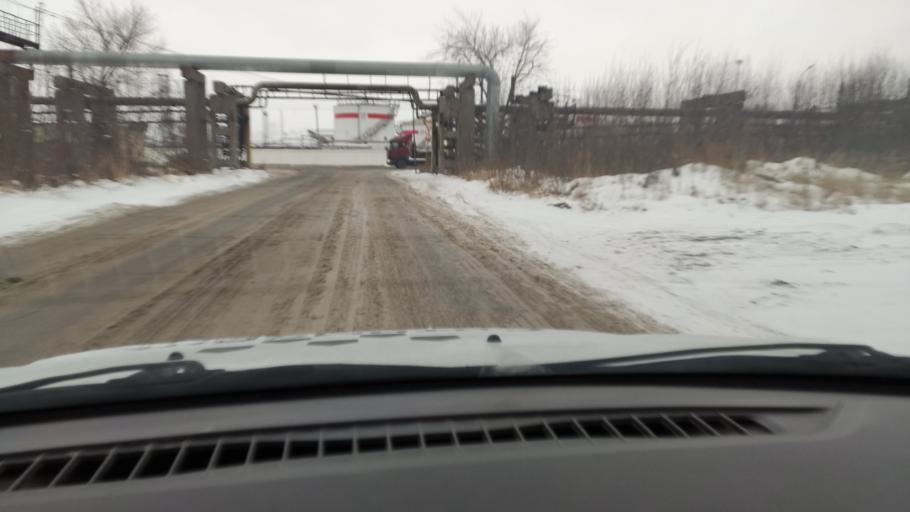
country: RU
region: Perm
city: Gamovo
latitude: 57.9196
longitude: 56.1482
